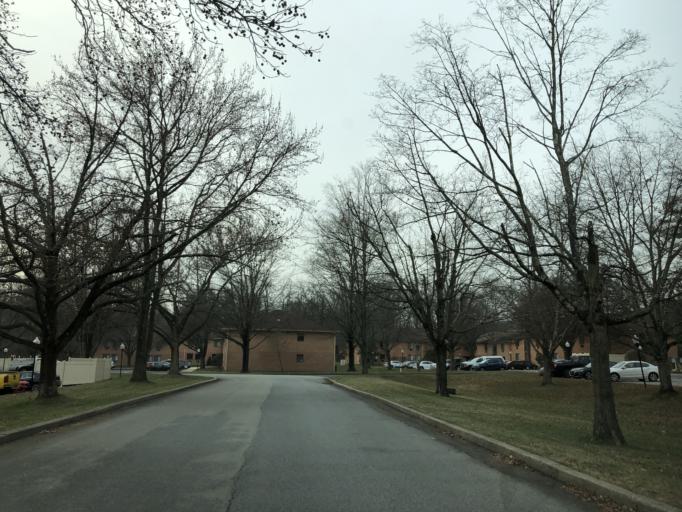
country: US
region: Pennsylvania
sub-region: Chester County
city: Exton
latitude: 40.0374
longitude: -75.6363
